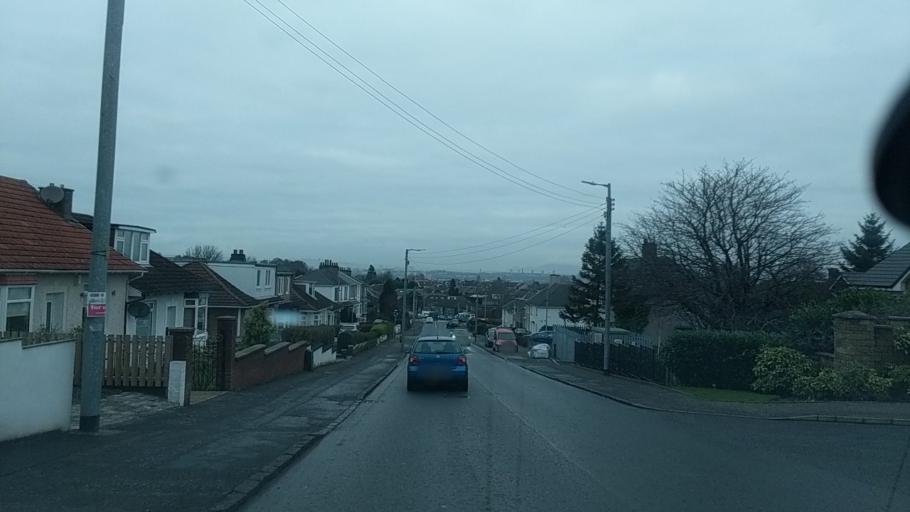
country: GB
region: Scotland
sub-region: South Lanarkshire
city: Rutherglen
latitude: 55.8169
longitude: -4.1892
